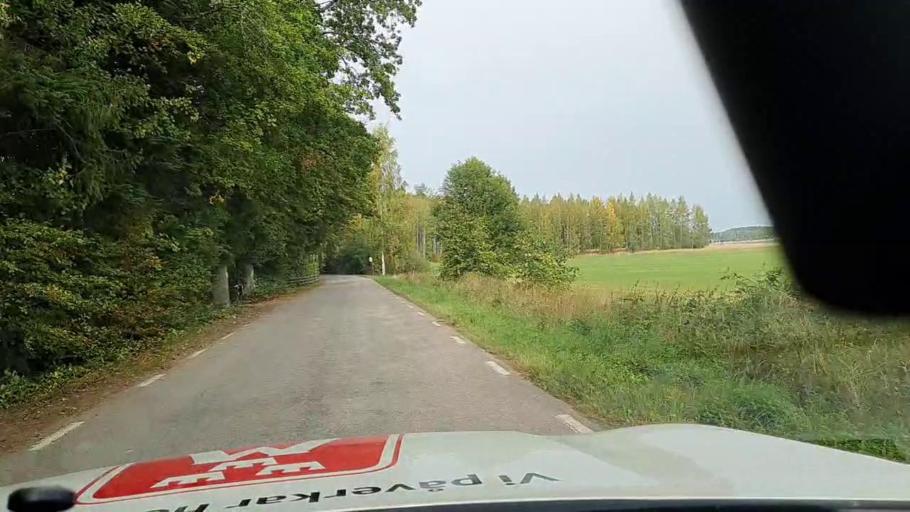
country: SE
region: Soedermanland
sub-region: Nykopings Kommun
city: Svalsta
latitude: 58.8290
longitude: 16.8838
